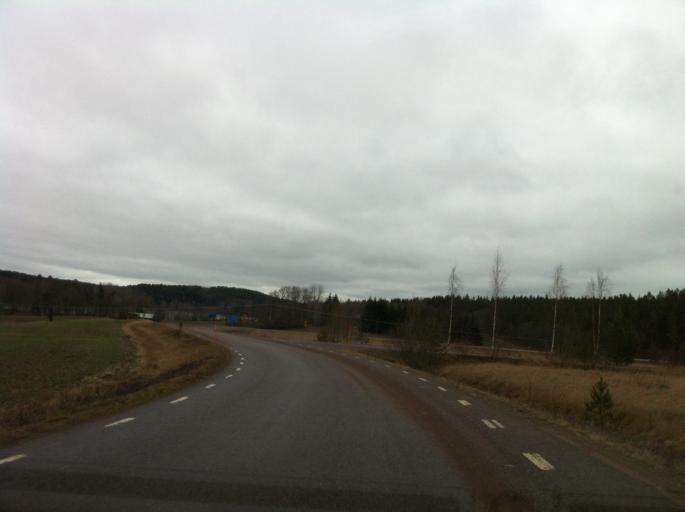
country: SE
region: Kalmar
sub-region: Vasterviks Kommun
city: Overum
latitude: 57.9021
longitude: 16.0858
